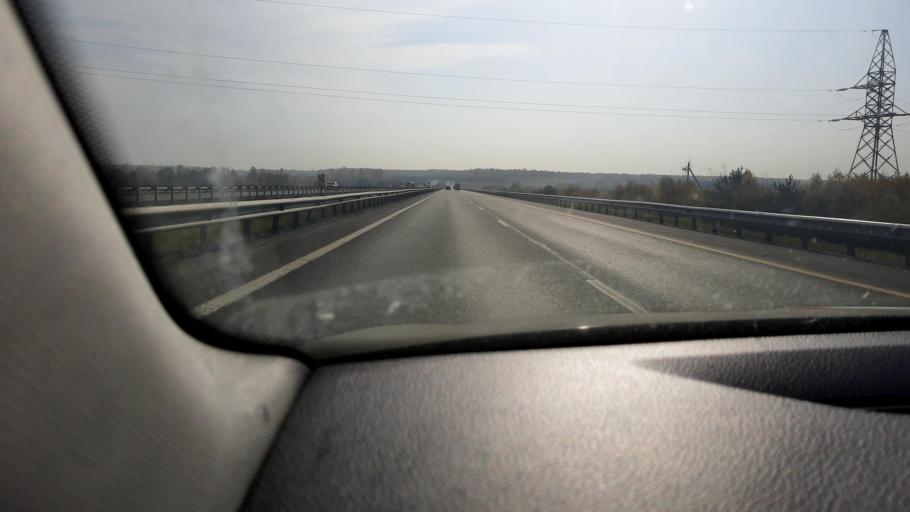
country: RU
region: Moskovskaya
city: Zhilevo
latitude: 55.0363
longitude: 37.9431
